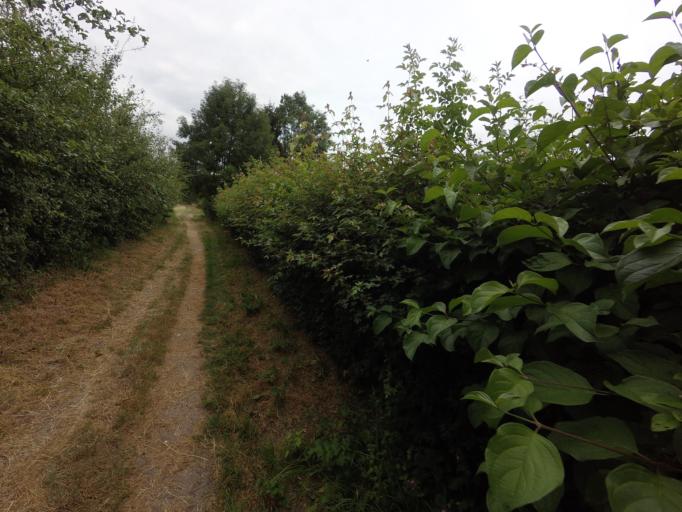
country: NL
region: Limburg
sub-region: Valkenburg aan de Geul
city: Schin op Geul
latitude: 50.8491
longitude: 5.8556
